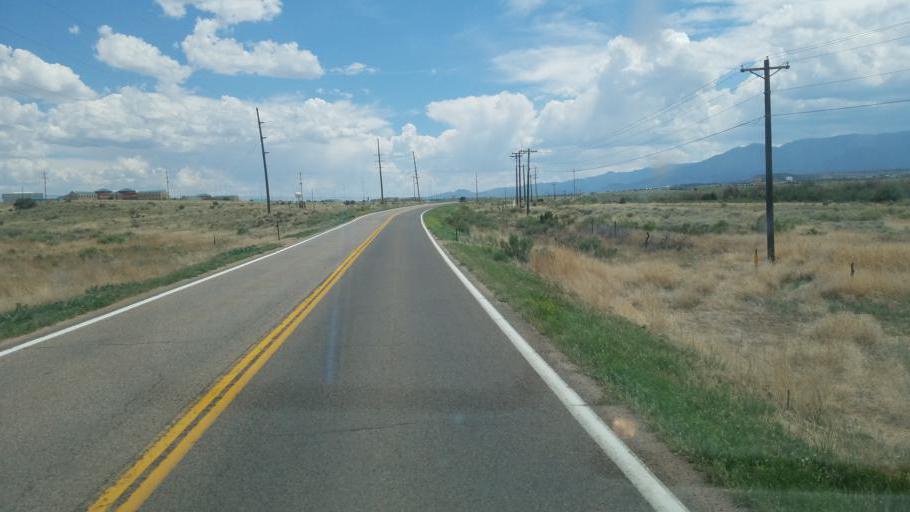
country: US
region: Colorado
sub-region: Fremont County
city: Florence
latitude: 38.3694
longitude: -105.1078
